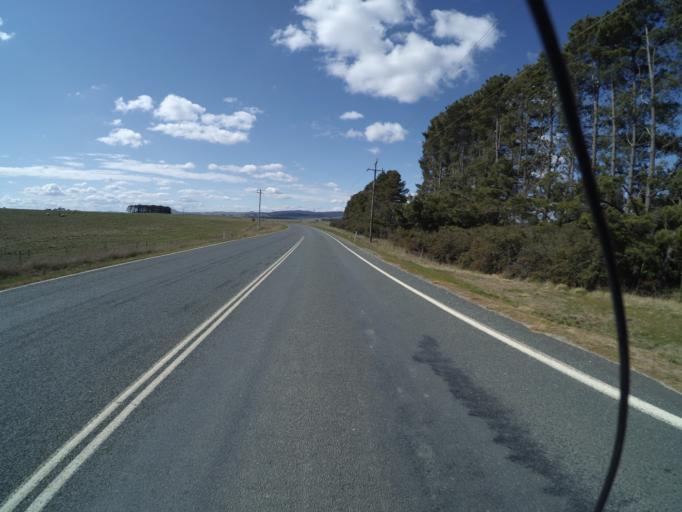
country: AU
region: New South Wales
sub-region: Palerang
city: Bungendore
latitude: -35.2195
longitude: 149.4631
